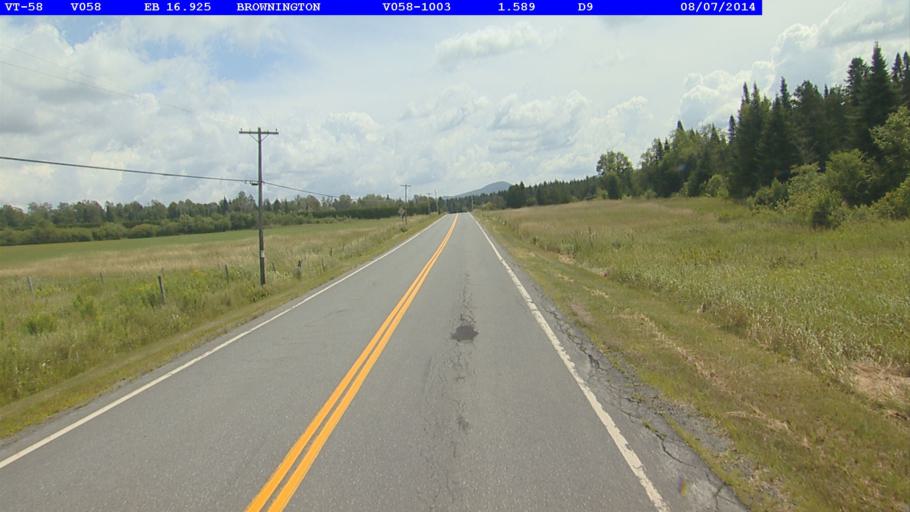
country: US
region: Vermont
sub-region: Orleans County
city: Newport
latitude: 44.7987
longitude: -72.1154
